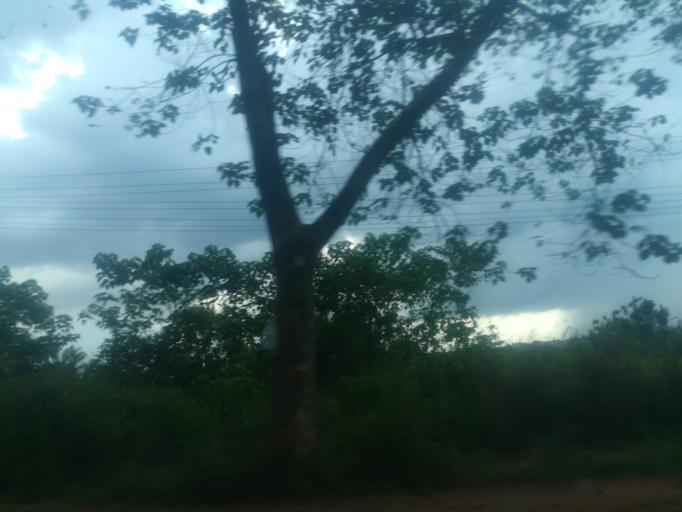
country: NG
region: Oyo
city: Ibadan
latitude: 7.4350
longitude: 3.8873
